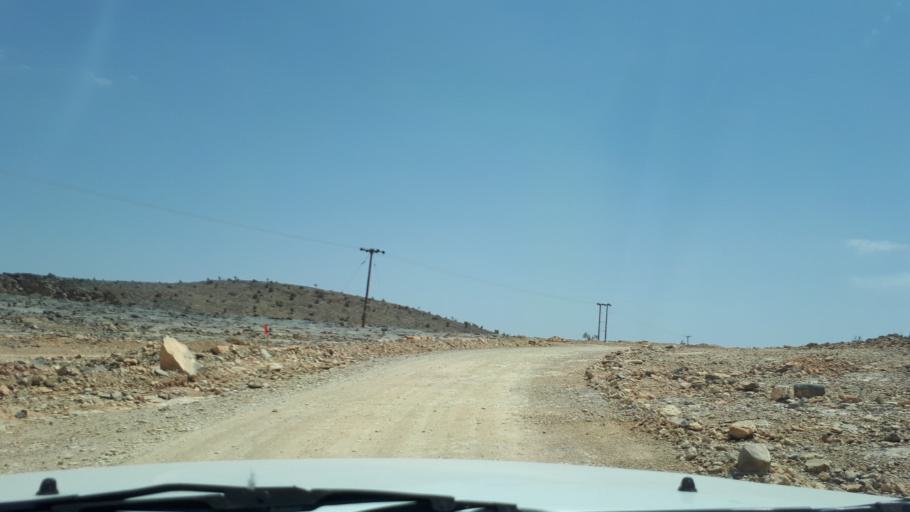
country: OM
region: Muhafazat ad Dakhiliyah
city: Bahla'
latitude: 23.2026
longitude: 57.2008
